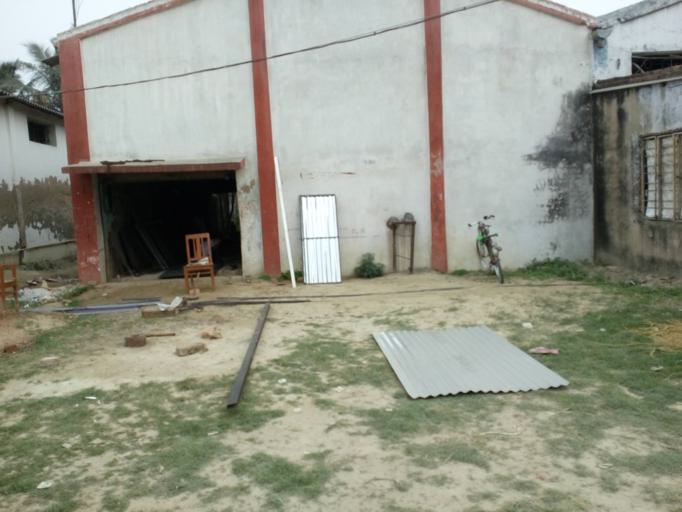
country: IN
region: Bihar
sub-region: Muzaffarpur
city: Muzaffarpur
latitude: 26.1011
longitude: 85.4098
